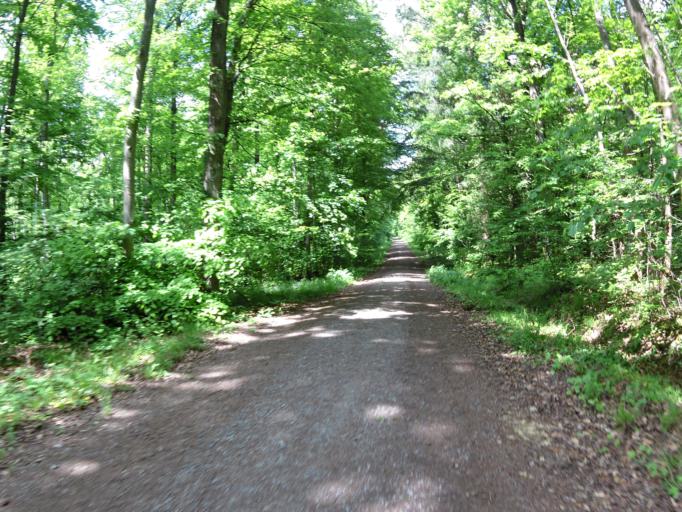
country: DE
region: Bavaria
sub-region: Regierungsbezirk Unterfranken
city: Kist
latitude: 49.7266
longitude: 9.8539
